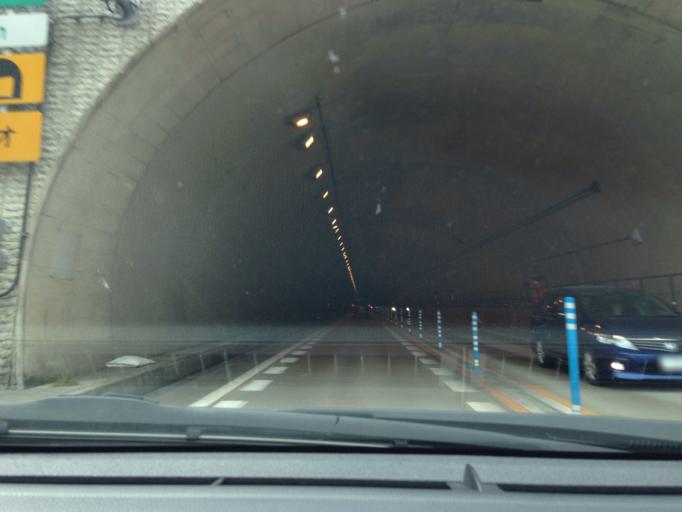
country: JP
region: Gifu
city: Takayama
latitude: 36.1606
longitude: 137.2217
